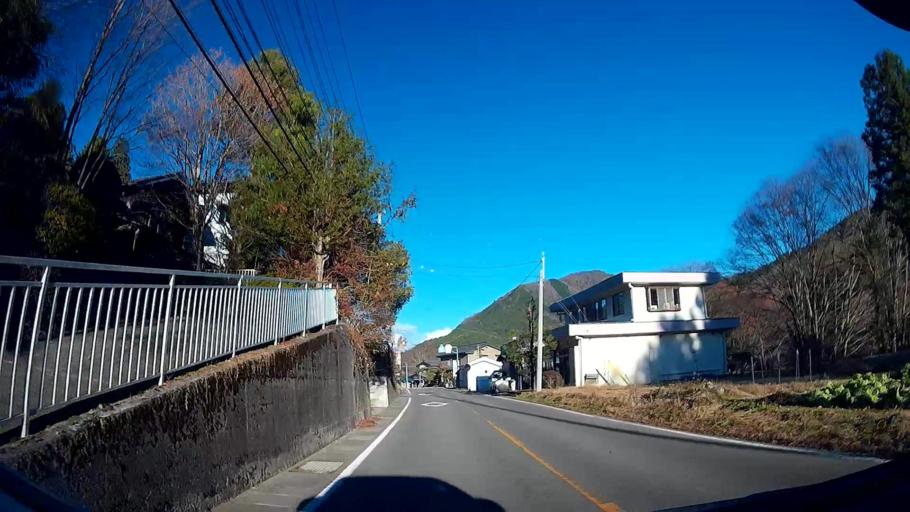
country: JP
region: Yamanashi
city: Otsuki
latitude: 35.4946
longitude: 138.9801
